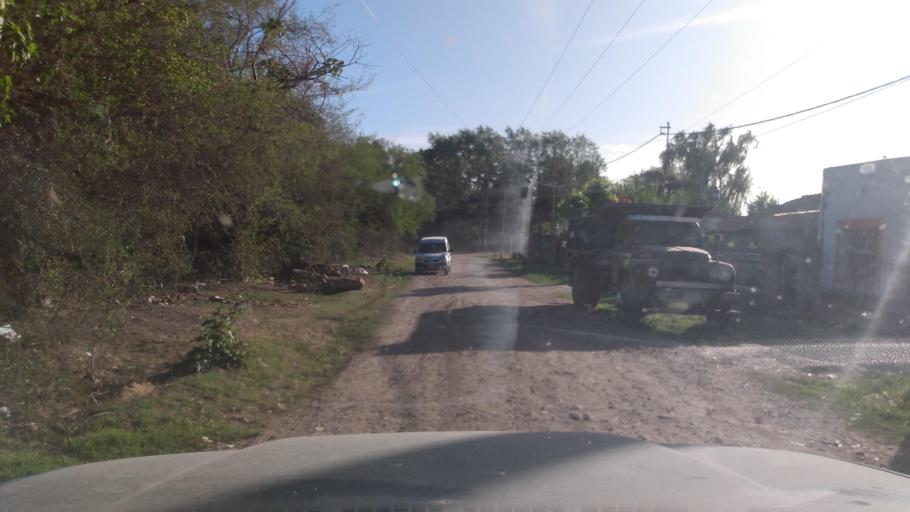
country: AR
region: Buenos Aires
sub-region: Partido de Lujan
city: Lujan
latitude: -34.5562
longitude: -59.1355
